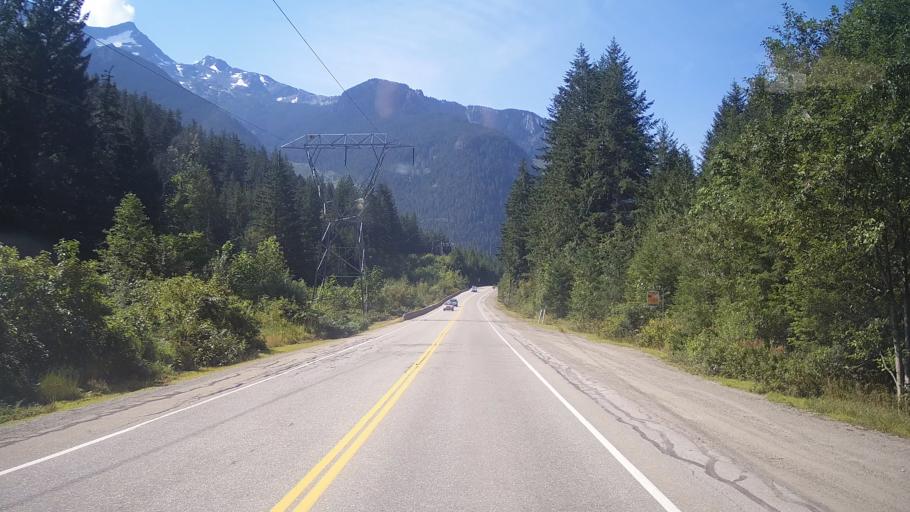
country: CA
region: British Columbia
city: Pemberton
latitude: 50.3055
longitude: -122.8090
